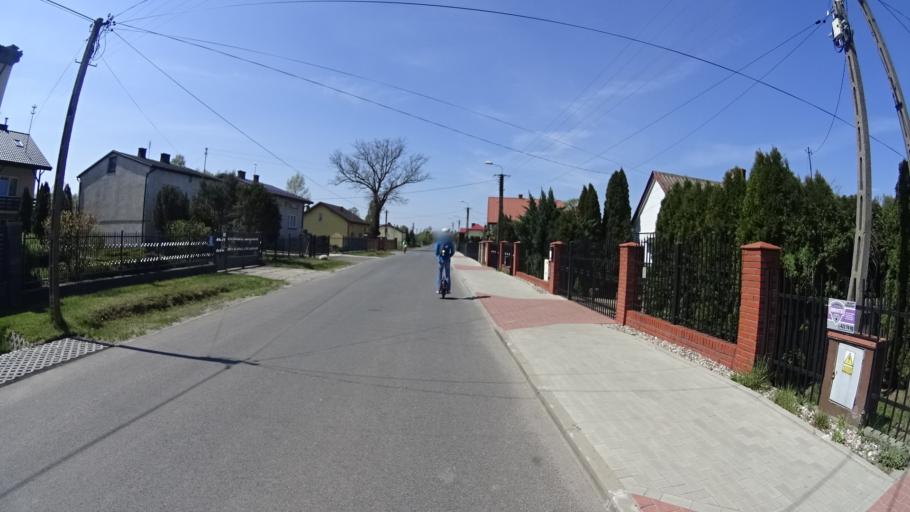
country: PL
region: Masovian Voivodeship
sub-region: Powiat warszawski zachodni
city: Truskaw
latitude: 52.2828
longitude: 20.7397
